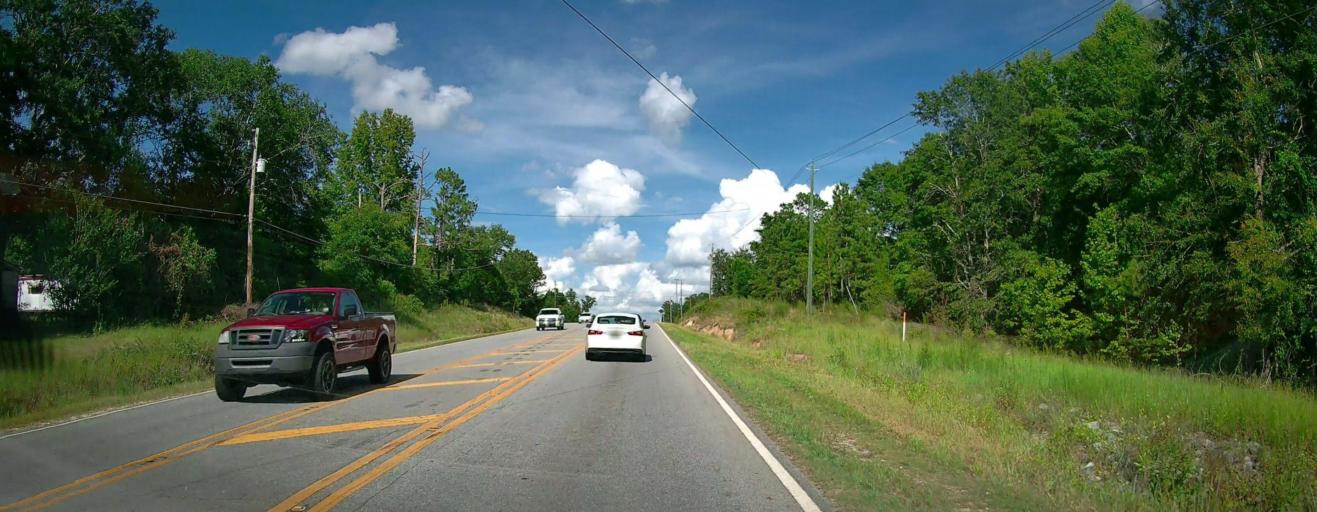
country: US
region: Alabama
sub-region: Russell County
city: Ladonia
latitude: 32.4674
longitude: -85.1082
